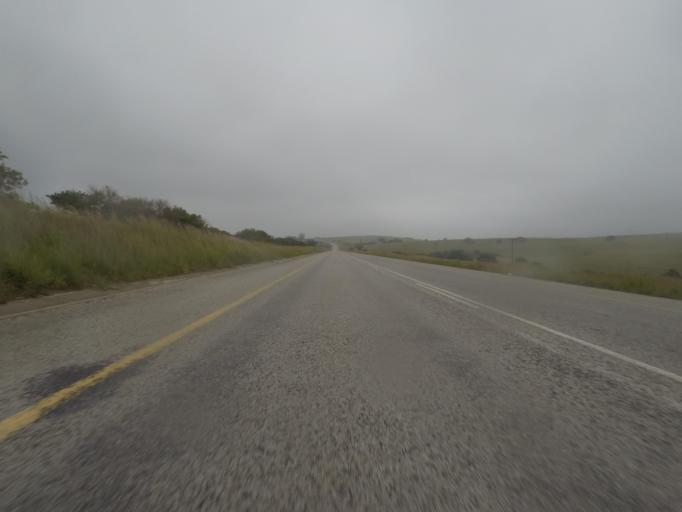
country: ZA
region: Eastern Cape
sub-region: Cacadu District Municipality
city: Grahamstown
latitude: -33.6308
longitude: 26.3136
